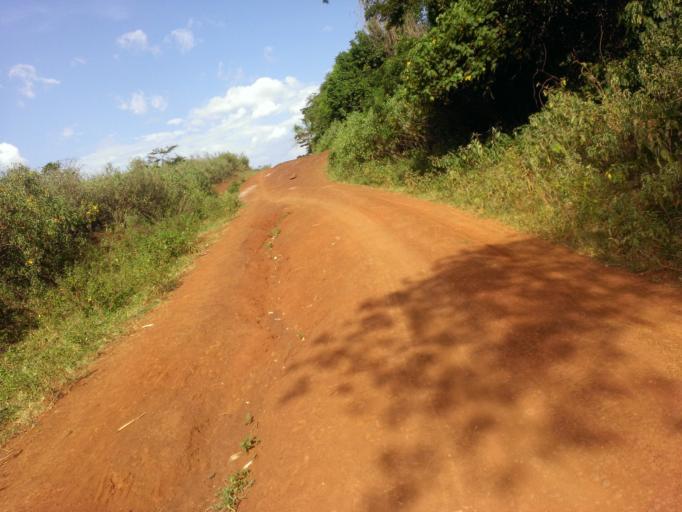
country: UG
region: Eastern Region
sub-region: Busia District
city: Busia
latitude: 0.5489
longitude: 34.0167
